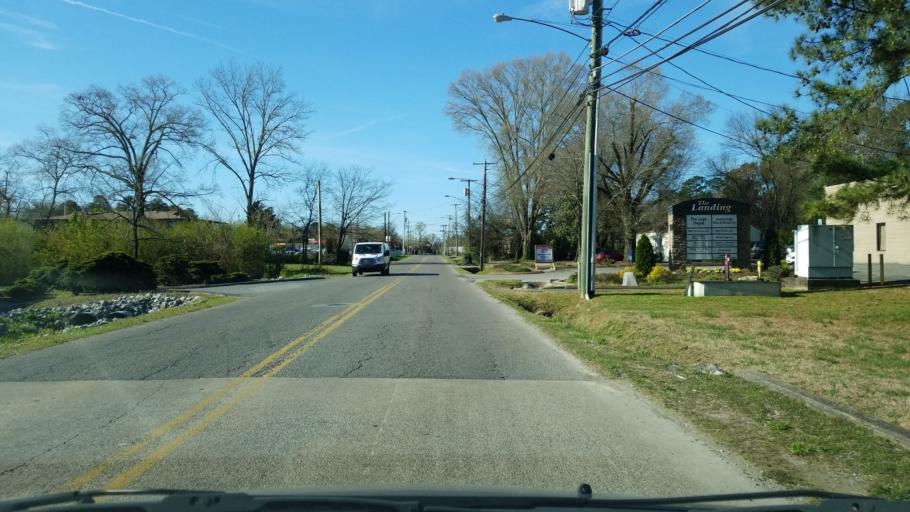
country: US
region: Tennessee
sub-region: Hamilton County
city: East Brainerd
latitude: 35.0255
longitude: -85.1970
